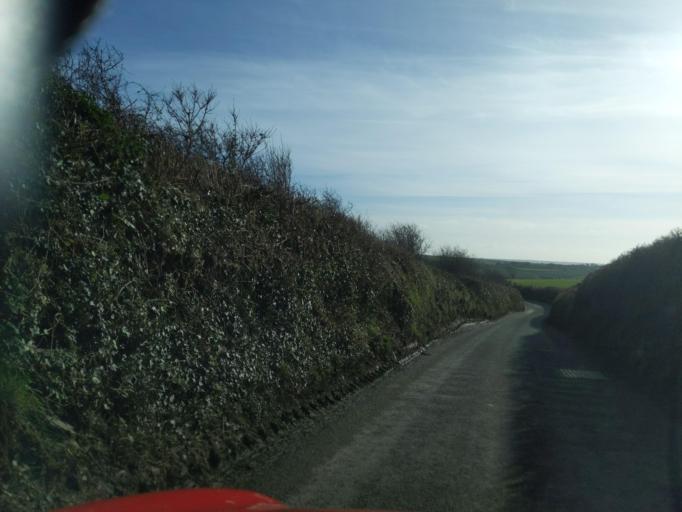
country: GB
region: England
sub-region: Devon
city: Kingsbridge
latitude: 50.3419
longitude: -3.7244
